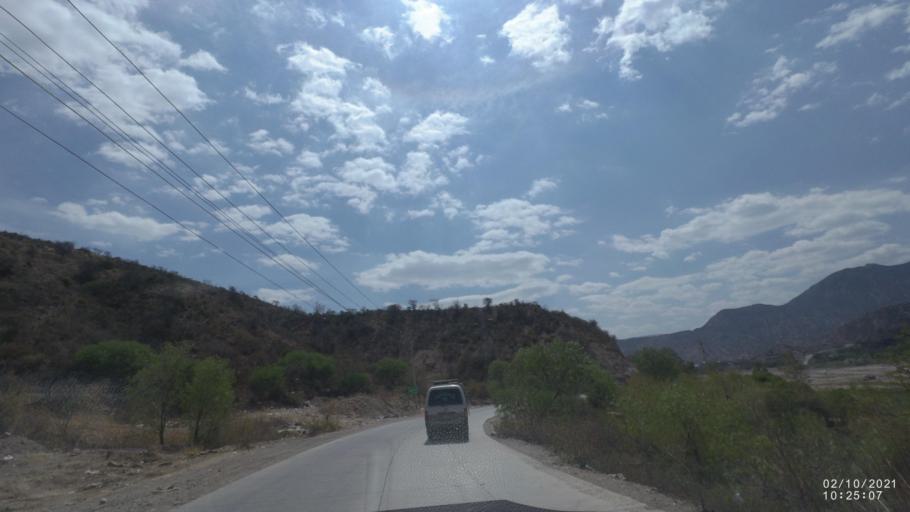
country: BO
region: Cochabamba
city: Irpa Irpa
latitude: -17.7244
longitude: -66.2701
